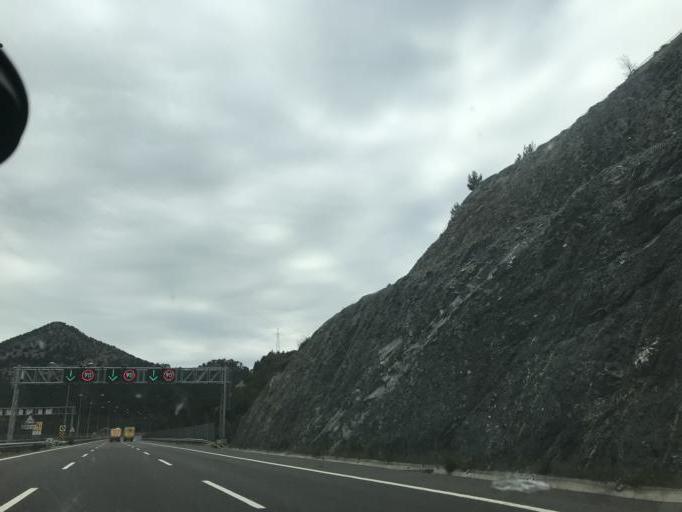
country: TR
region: Nigde
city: Ciftehan
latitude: 37.5018
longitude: 34.8245
